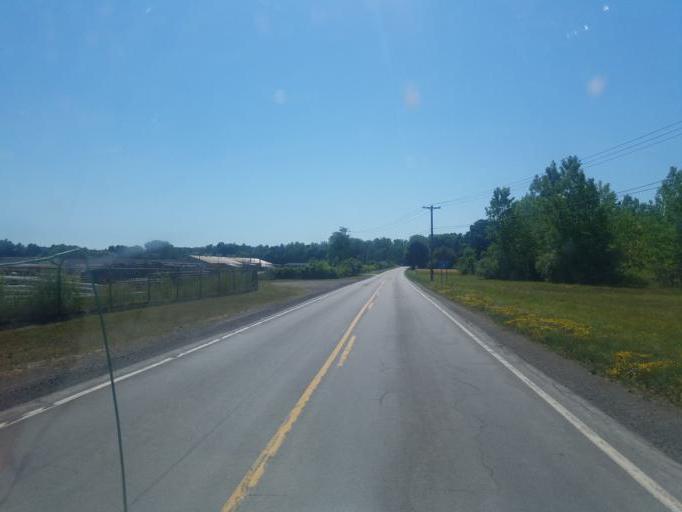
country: US
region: New York
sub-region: Ontario County
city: Phelps
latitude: 42.9328
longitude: -77.0022
